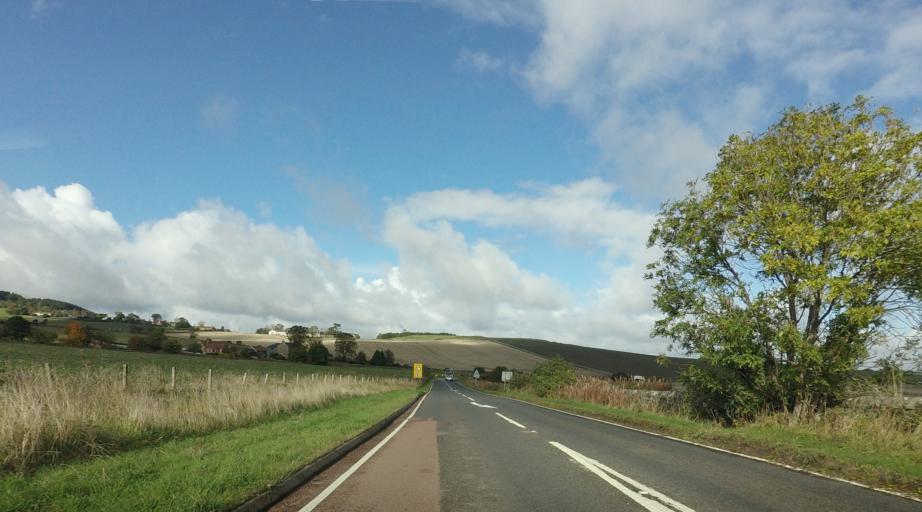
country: GB
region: Scotland
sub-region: Fife
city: Balmullo
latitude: 56.3818
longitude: -2.9229
